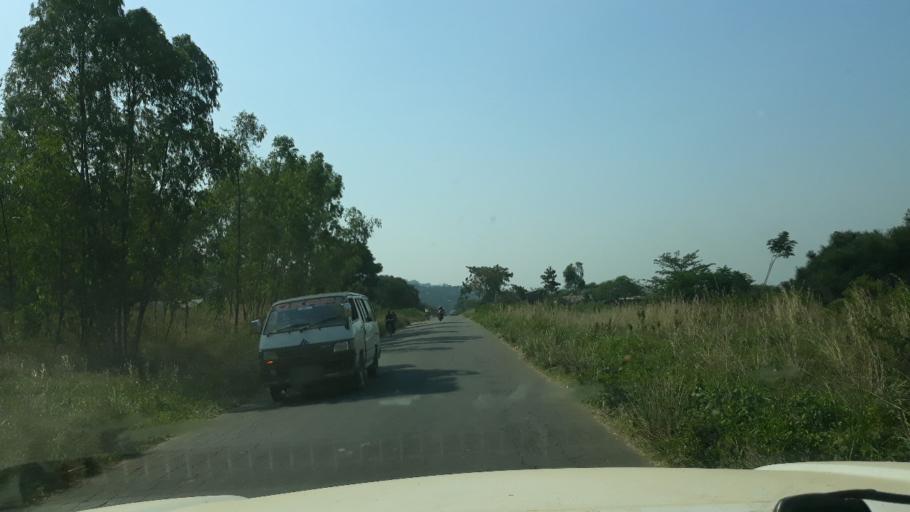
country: CD
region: South Kivu
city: Uvira
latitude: -3.2512
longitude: 29.1613
